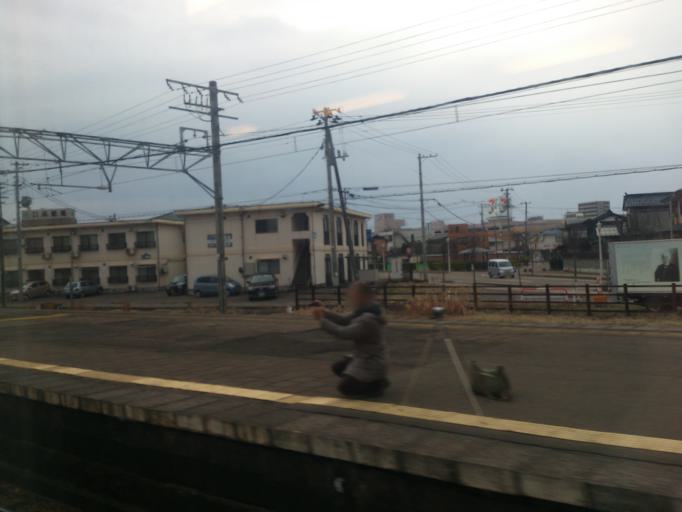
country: JP
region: Niigata
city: Joetsu
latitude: 37.1698
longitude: 138.2411
